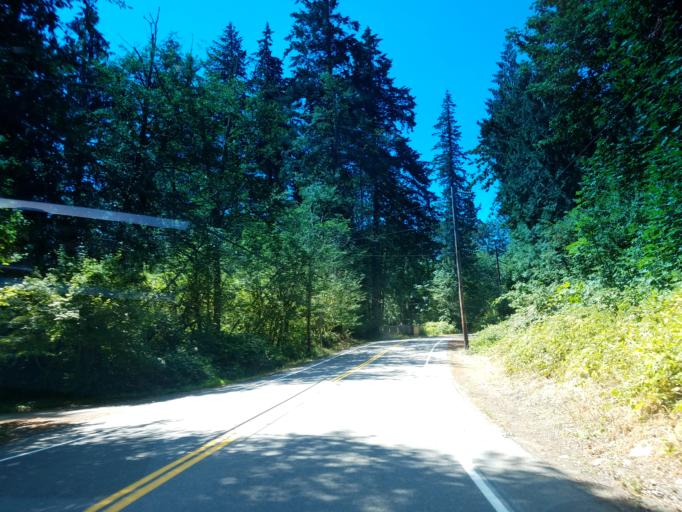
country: US
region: Washington
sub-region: King County
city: Union Hill-Novelty Hill
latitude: 47.6614
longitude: -122.0098
